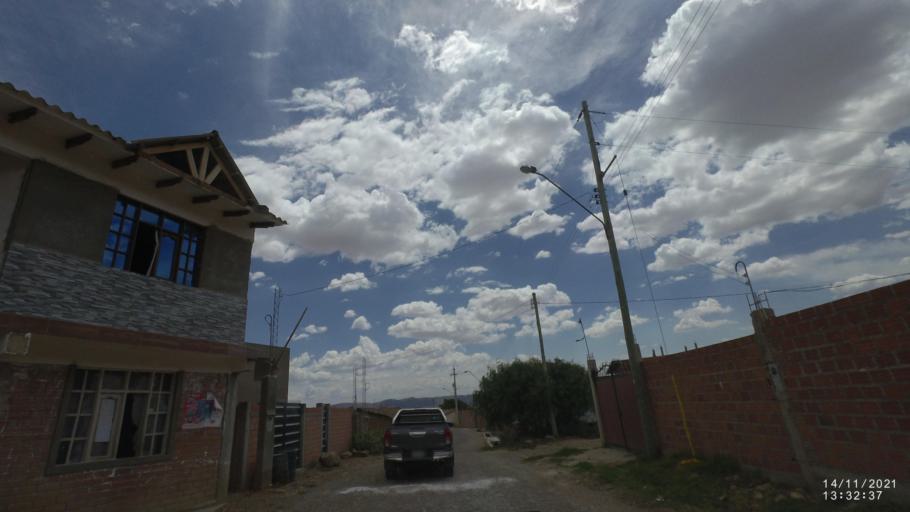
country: BO
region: Cochabamba
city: Colomi
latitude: -17.3970
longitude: -65.9841
